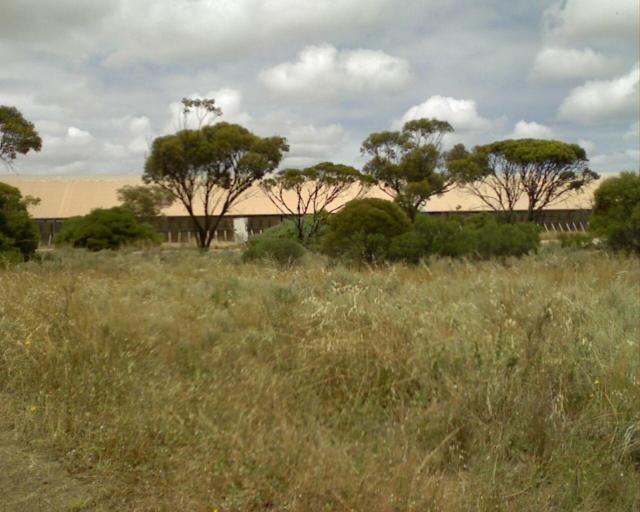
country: AU
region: South Australia
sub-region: Ceduna
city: Ceduna
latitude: -31.9296
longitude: 133.0090
